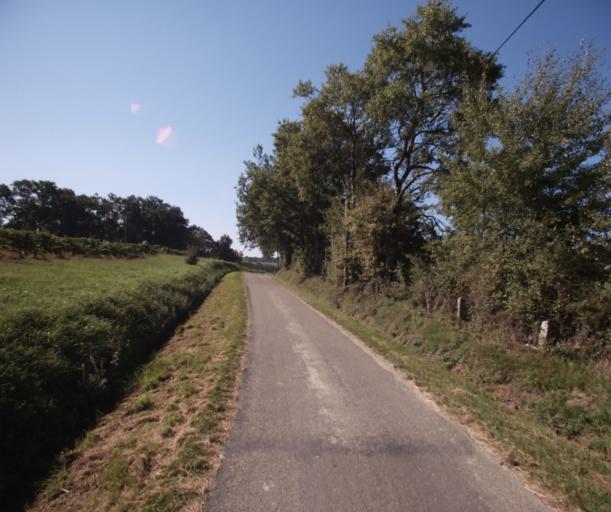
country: FR
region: Midi-Pyrenees
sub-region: Departement du Gers
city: Cazaubon
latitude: 43.9404
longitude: -0.0363
